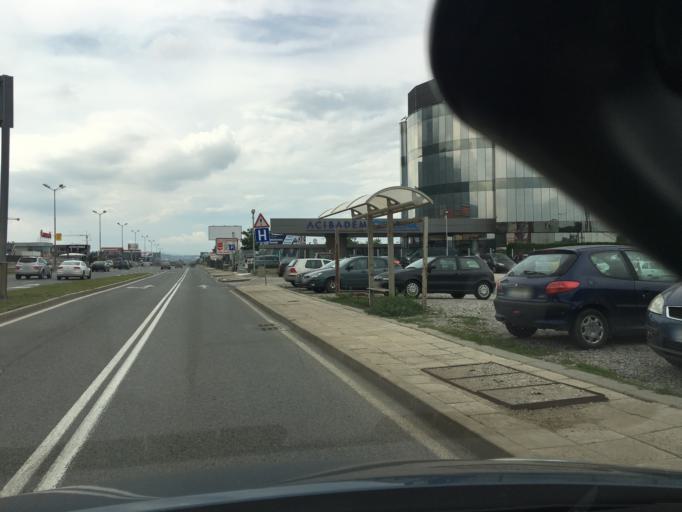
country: BG
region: Sofia-Capital
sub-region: Stolichna Obshtina
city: Sofia
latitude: 42.6393
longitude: 23.3186
